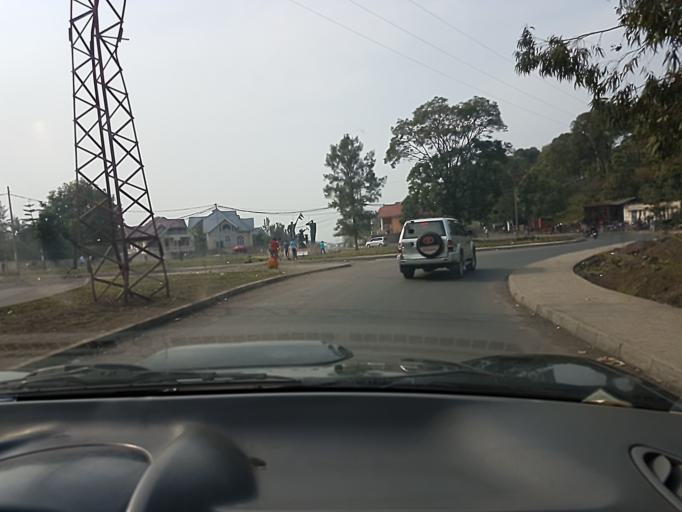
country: CD
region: Nord Kivu
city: Goma
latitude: -1.6824
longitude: 29.2285
